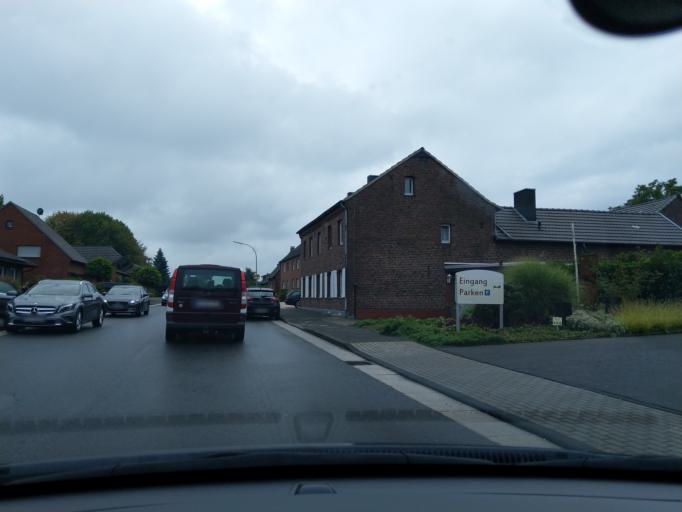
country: DE
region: North Rhine-Westphalia
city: Wegberg
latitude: 51.1273
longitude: 6.2868
